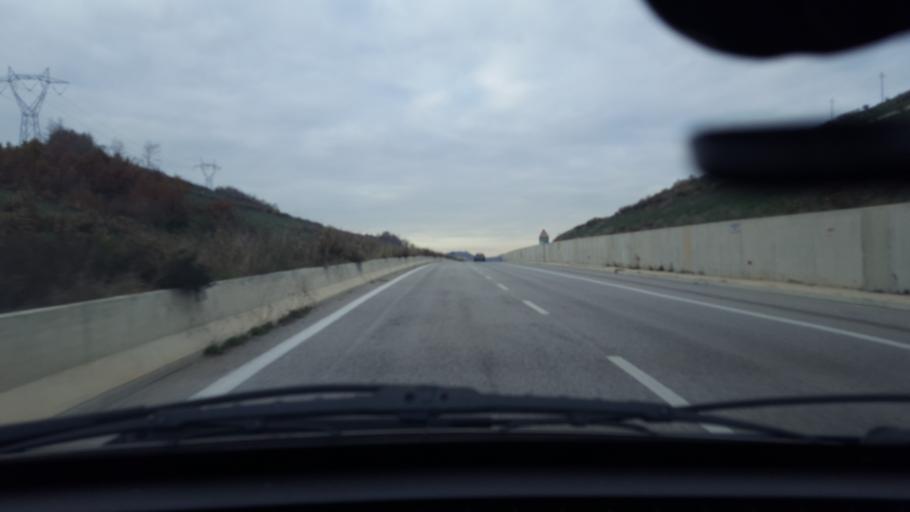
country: AL
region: Tirane
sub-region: Rrethi i Tiranes
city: Petrele
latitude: 41.2674
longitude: 19.8656
